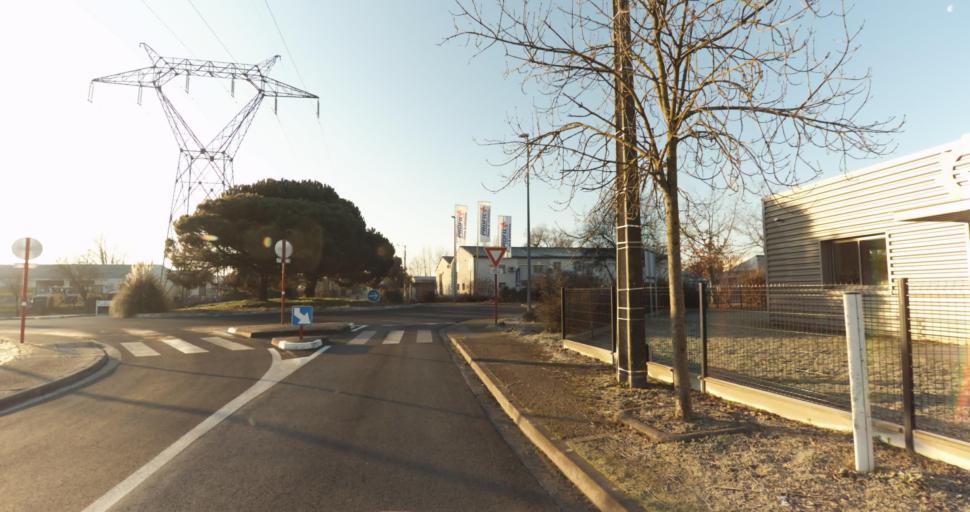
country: FR
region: Aquitaine
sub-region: Departement de la Gironde
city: Ambares-et-Lagrave
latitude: 44.9137
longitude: -0.4921
